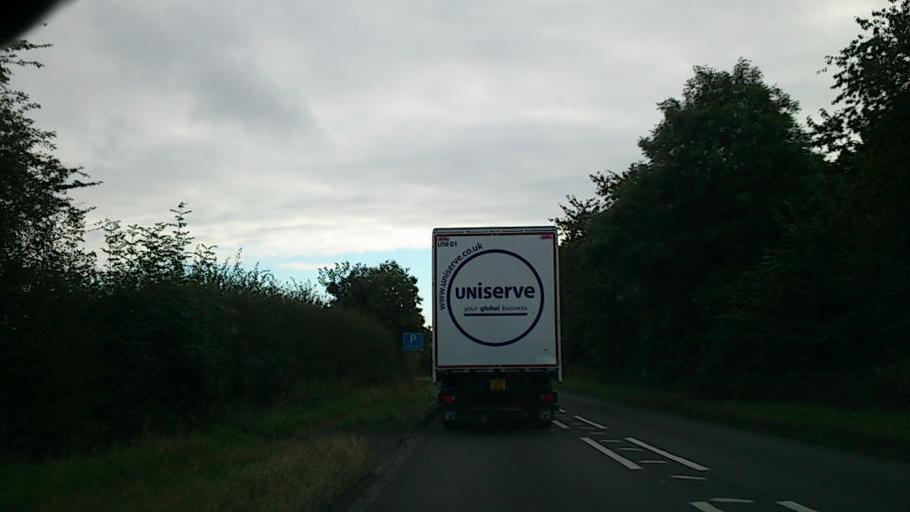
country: GB
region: England
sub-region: Shropshire
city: Ford
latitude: 52.7164
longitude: -2.8311
